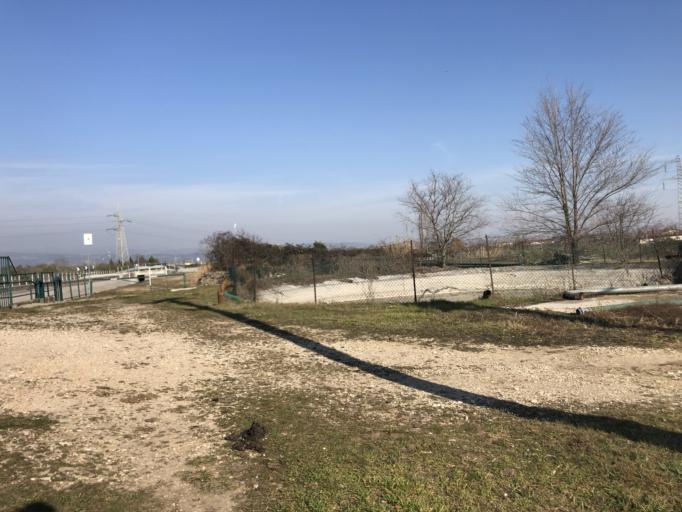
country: IT
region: Veneto
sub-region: Provincia di Verona
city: Lugagnano
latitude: 45.4207
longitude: 10.8804
